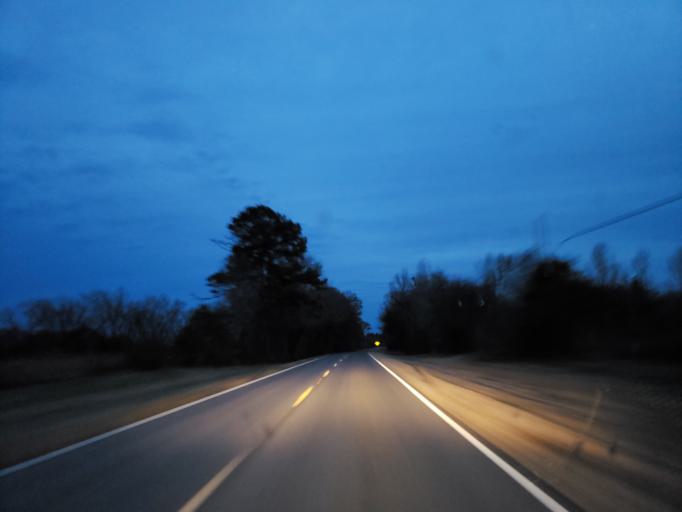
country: US
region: Alabama
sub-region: Greene County
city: Eutaw
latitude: 32.8885
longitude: -87.9452
